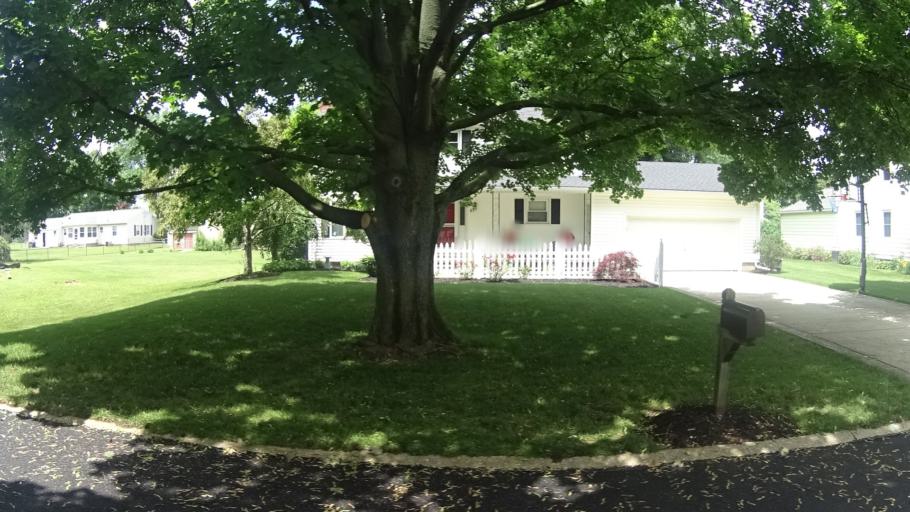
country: US
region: Ohio
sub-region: Erie County
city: Milan
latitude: 41.2881
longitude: -82.6017
